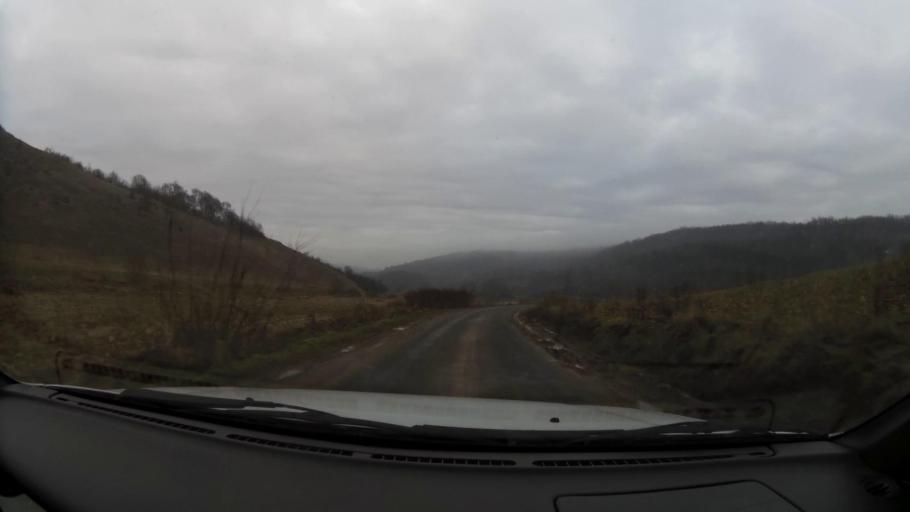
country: HU
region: Borsod-Abauj-Zemplen
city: Rudabanya
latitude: 48.4053
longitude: 20.6461
